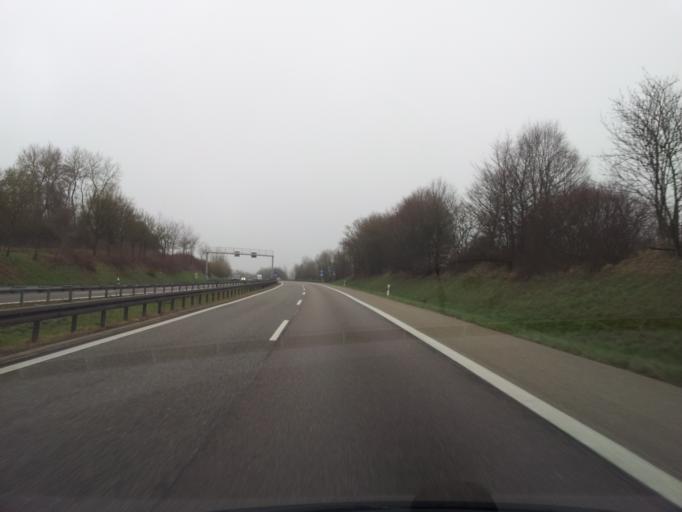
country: DE
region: Baden-Wuerttemberg
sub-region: Freiburg Region
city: Singen
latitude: 47.7713
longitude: 8.8148
